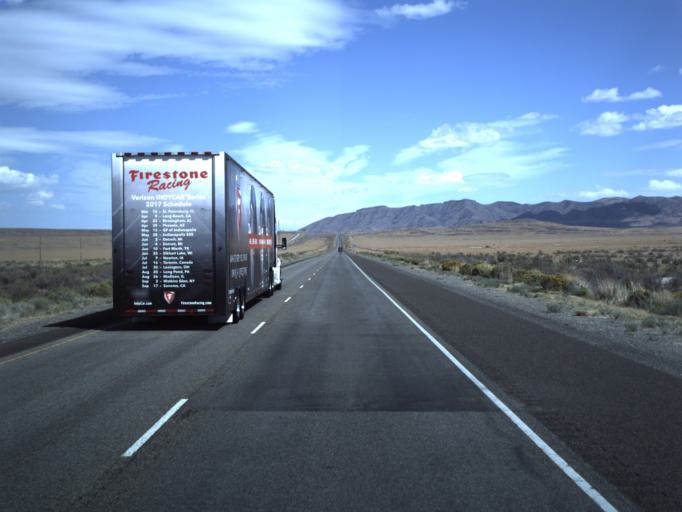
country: US
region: Utah
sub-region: Tooele County
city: Grantsville
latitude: 40.7481
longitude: -113.0532
